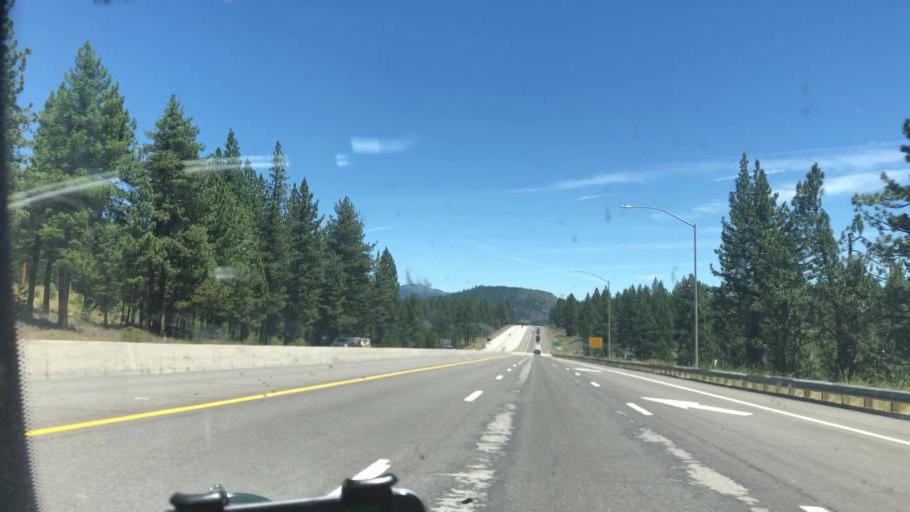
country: US
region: California
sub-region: Nevada County
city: Truckee
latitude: 39.3431
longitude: -120.1612
